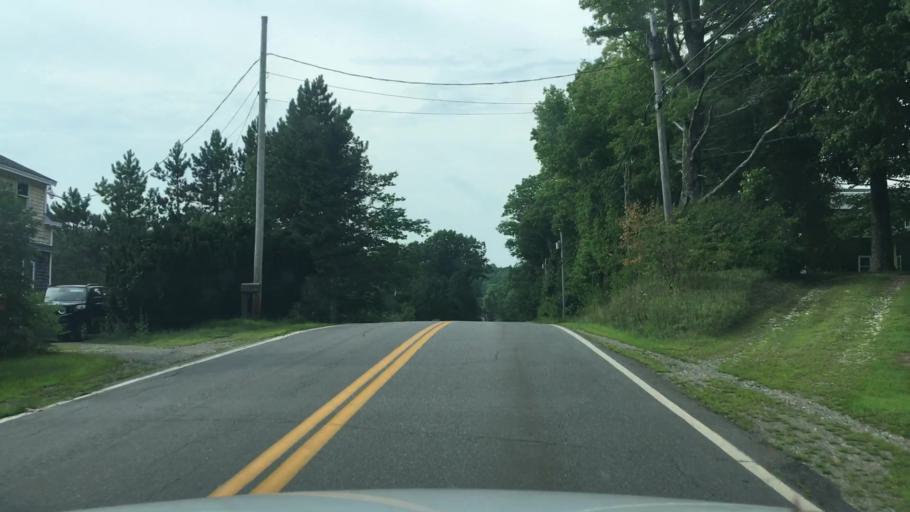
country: US
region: Maine
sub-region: Lincoln County
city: Jefferson
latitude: 44.1926
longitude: -69.3777
